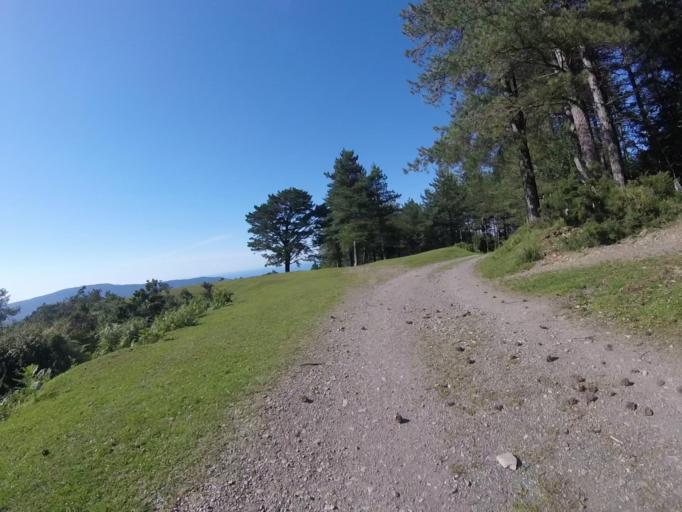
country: ES
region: Basque Country
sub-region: Provincia de Guipuzcoa
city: Irun
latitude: 43.3032
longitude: -1.7823
